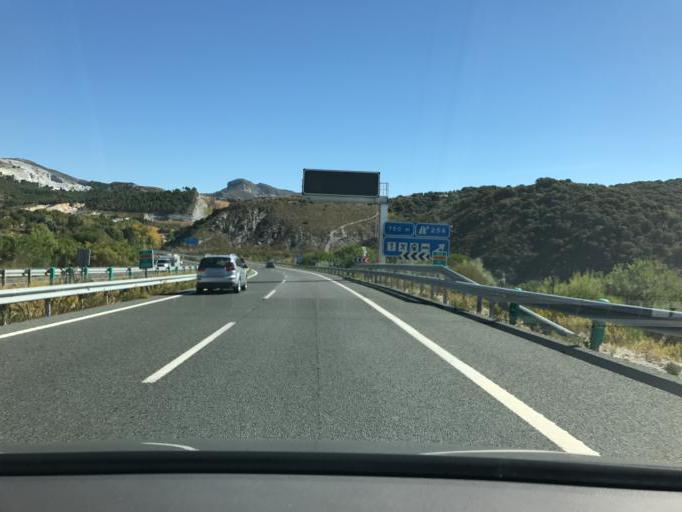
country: ES
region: Andalusia
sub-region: Provincia de Granada
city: Huetor Santillan
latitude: 37.2274
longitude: -3.5076
